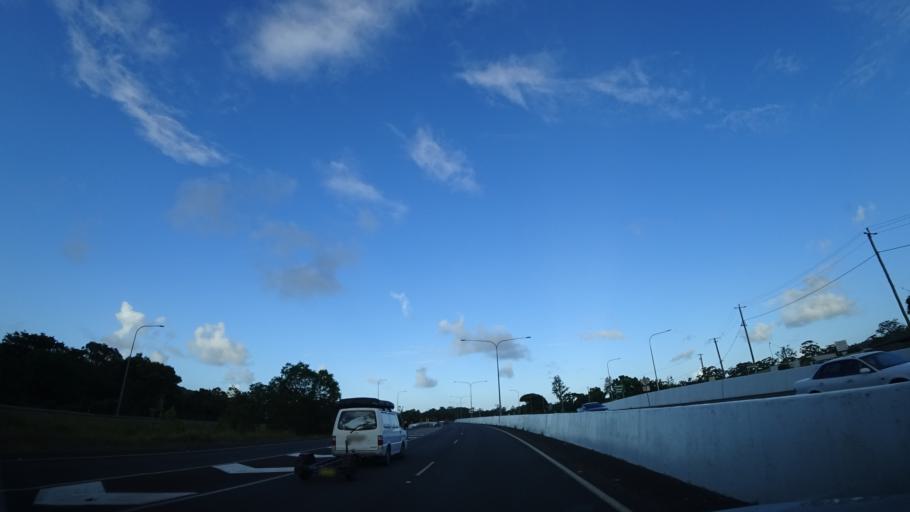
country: AU
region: Queensland
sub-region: Sunshine Coast
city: Woombye
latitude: -26.6735
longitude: 153.0032
